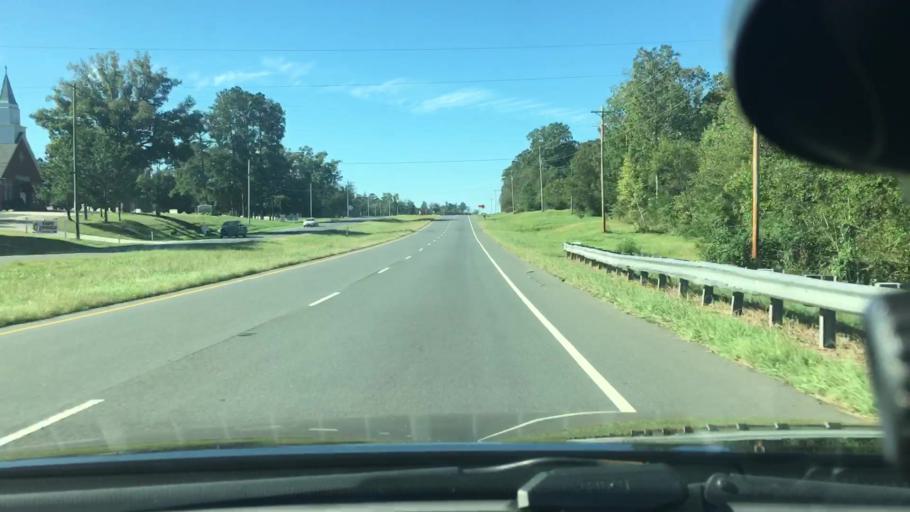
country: US
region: North Carolina
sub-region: Stanly County
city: Albemarle
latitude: 35.3210
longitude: -80.2487
